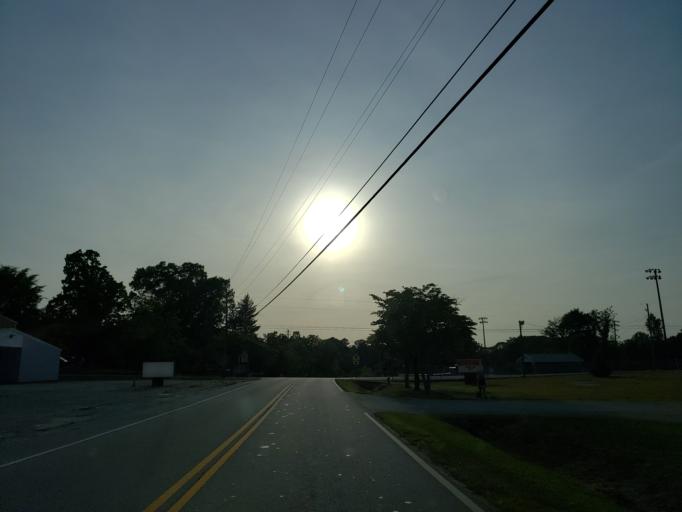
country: US
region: Georgia
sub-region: Carroll County
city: Mount Zion
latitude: 33.6343
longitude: -85.1866
